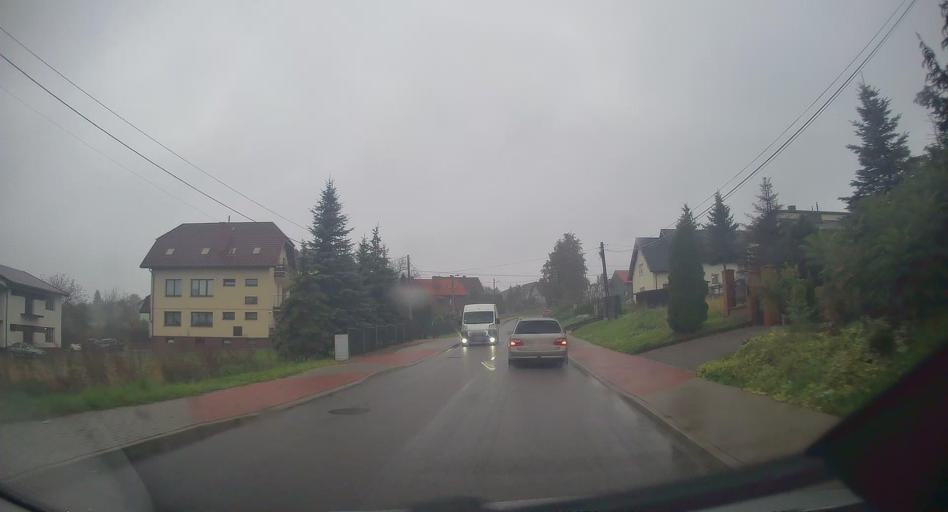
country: PL
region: Lesser Poland Voivodeship
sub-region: Powiat krakowski
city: Ochojno
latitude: 49.9542
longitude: 19.9764
